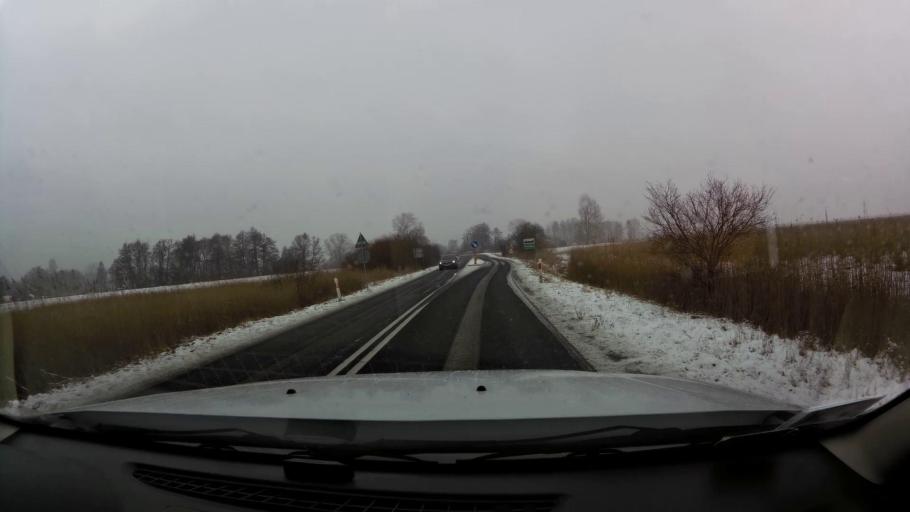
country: PL
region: West Pomeranian Voivodeship
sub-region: Powiat gryficki
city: Mrzezyno
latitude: 54.1333
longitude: 15.2823
